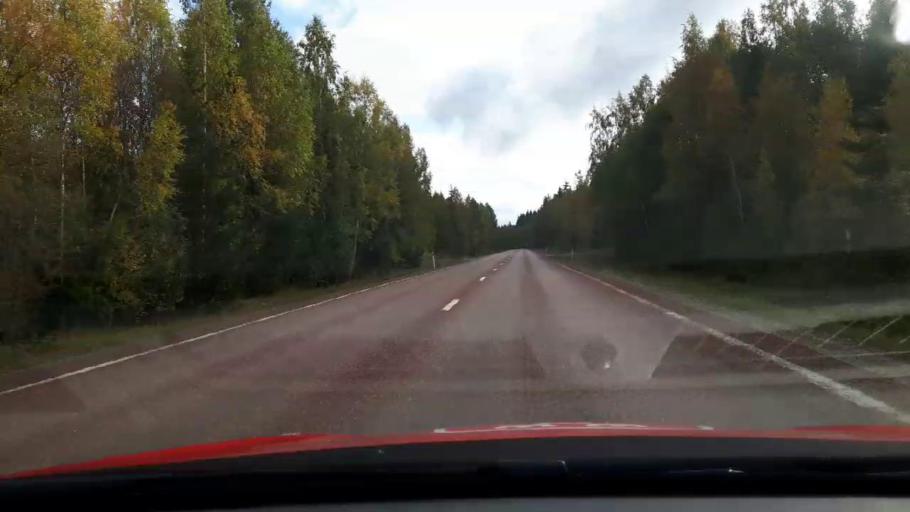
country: SE
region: Gaevleborg
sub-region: Ljusdals Kommun
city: Jaervsoe
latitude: 61.6409
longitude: 16.2323
